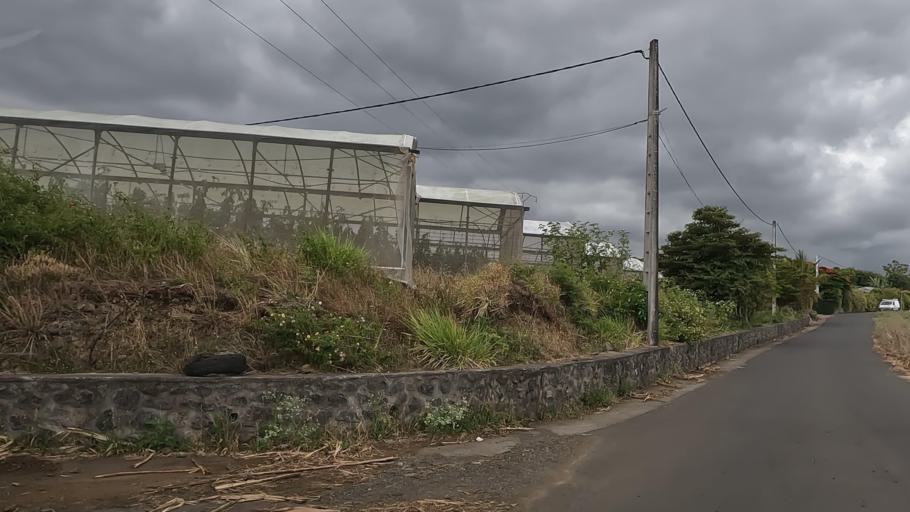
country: RE
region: Reunion
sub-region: Reunion
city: Saint-Pierre
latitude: -21.3409
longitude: 55.5198
